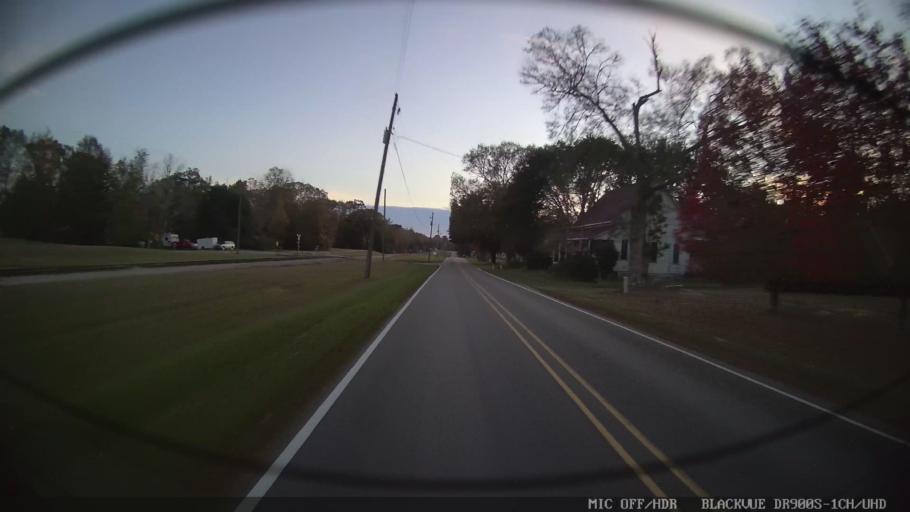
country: US
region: Mississippi
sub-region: Perry County
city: New Augusta
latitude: 31.0626
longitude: -89.1872
